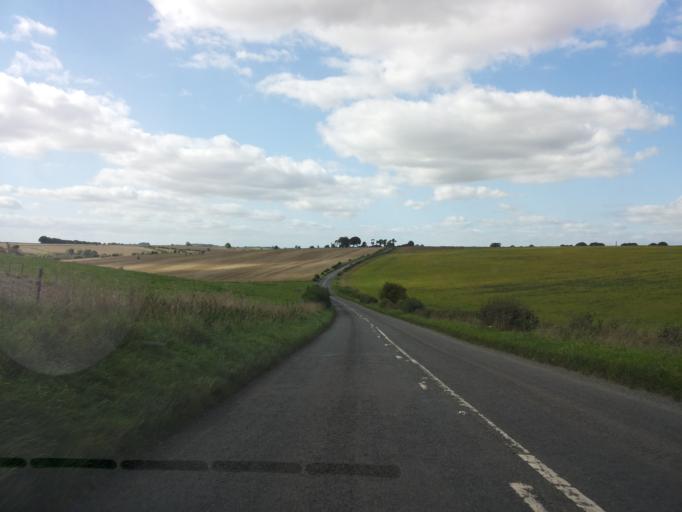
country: GB
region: England
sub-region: Wiltshire
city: Shrewton
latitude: 51.1865
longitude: -1.8737
